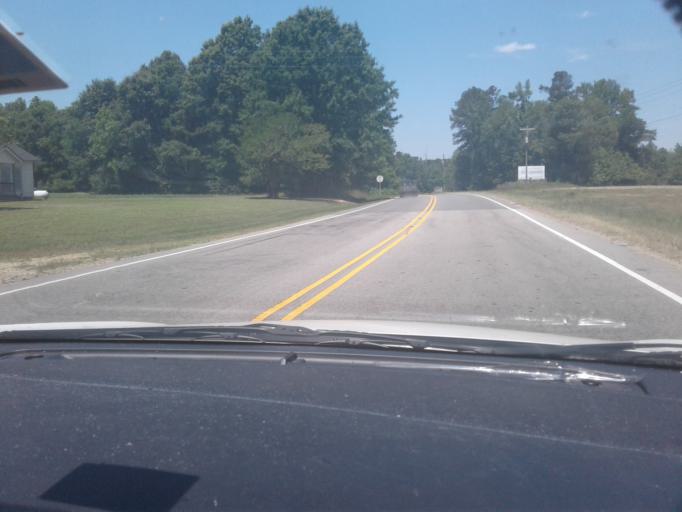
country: US
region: North Carolina
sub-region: Harnett County
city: Lillington
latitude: 35.4264
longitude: -78.8172
